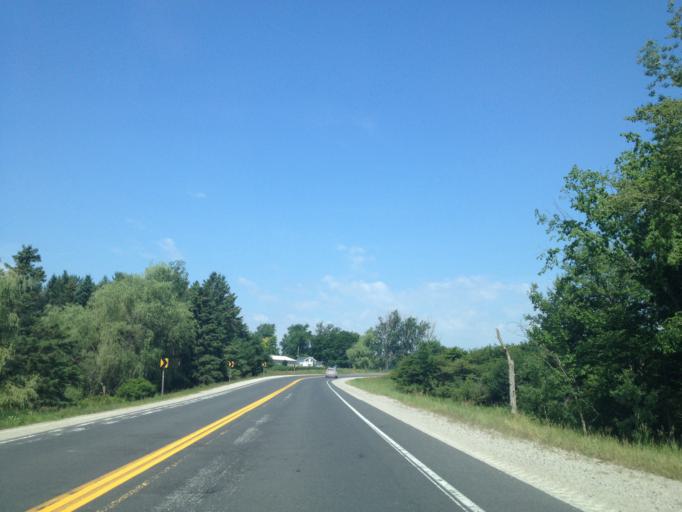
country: CA
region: Ontario
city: Huron East
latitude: 43.3731
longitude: -81.2152
